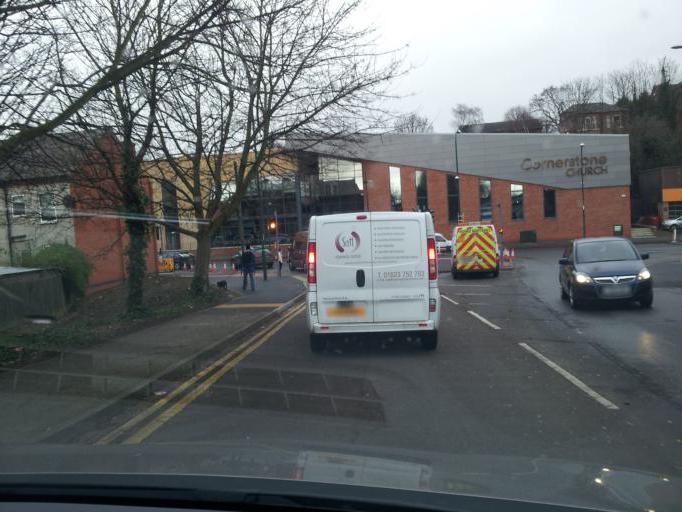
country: GB
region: England
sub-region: Nottingham
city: Nottingham
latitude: 52.9464
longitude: -1.1677
